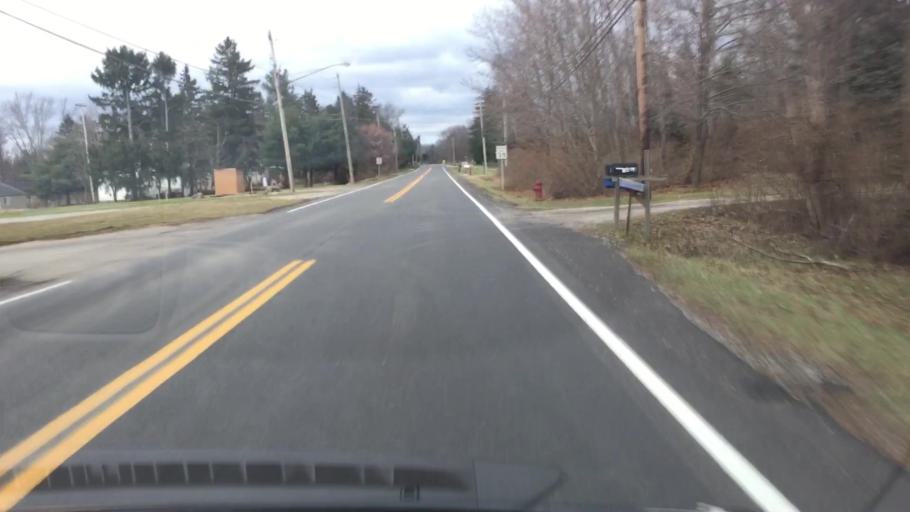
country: US
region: Ohio
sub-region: Summit County
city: Boston Heights
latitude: 41.2703
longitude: -81.5135
